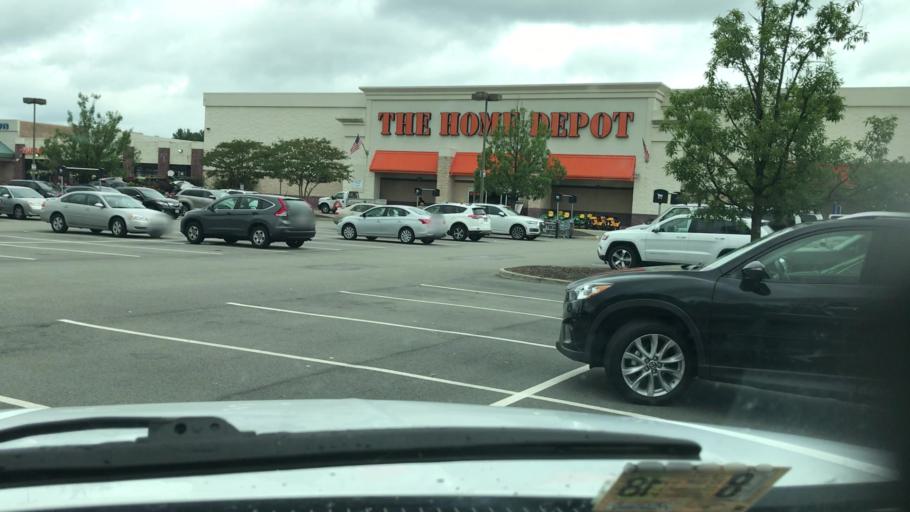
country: US
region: Virginia
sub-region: Henrico County
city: Short Pump
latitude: 37.6510
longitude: -77.6035
